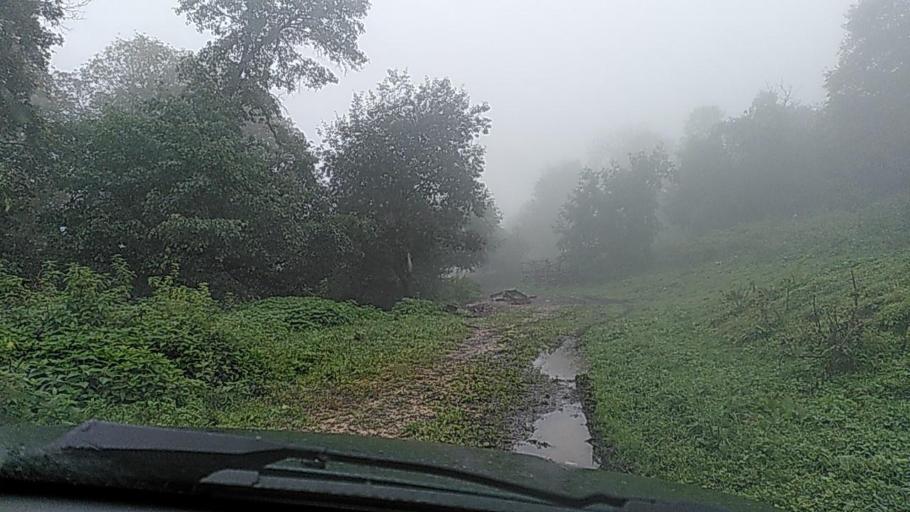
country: RU
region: Kabardino-Balkariya
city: Belaya Rechka
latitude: 43.3565
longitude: 43.3986
